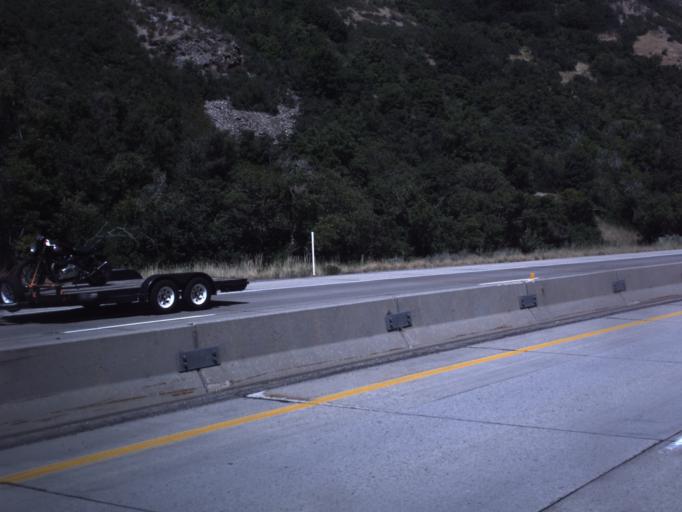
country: US
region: Utah
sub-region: Utah County
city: Orem
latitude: 40.3507
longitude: -111.5874
